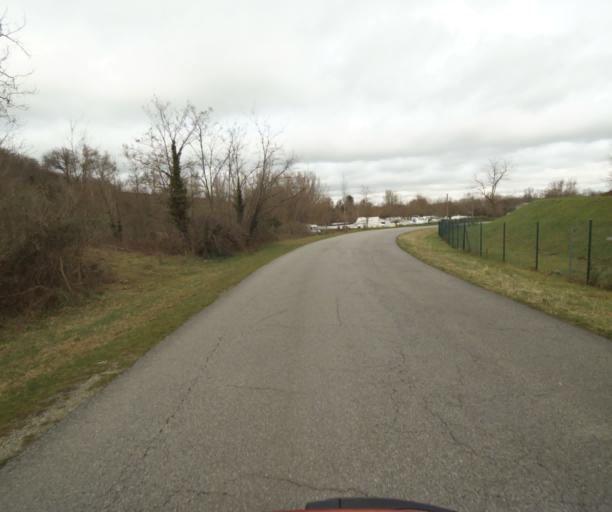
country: FR
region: Midi-Pyrenees
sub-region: Departement de l'Ariege
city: Pamiers
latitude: 43.1206
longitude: 1.5973
